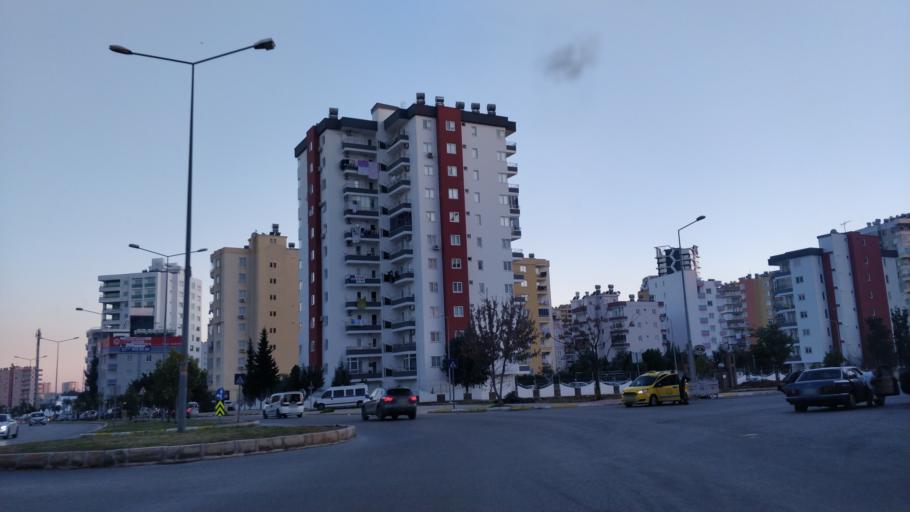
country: TR
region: Mersin
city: Mercin
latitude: 36.7925
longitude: 34.5883
